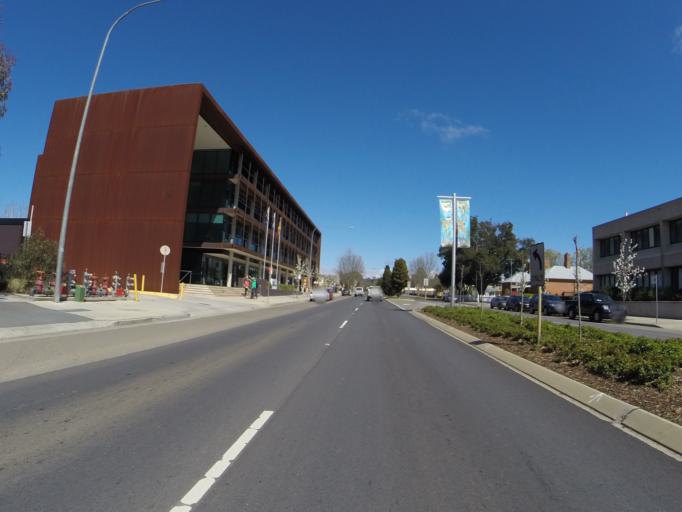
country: AU
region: New South Wales
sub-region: Queanbeyan
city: Queanbeyan
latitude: -35.3547
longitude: 149.2317
